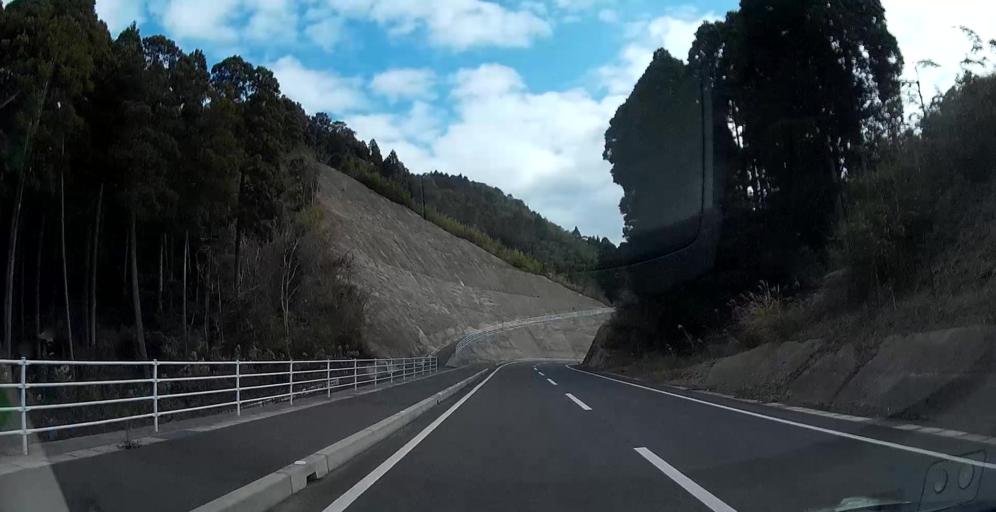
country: JP
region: Kumamoto
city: Minamata
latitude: 32.2322
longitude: 130.4252
